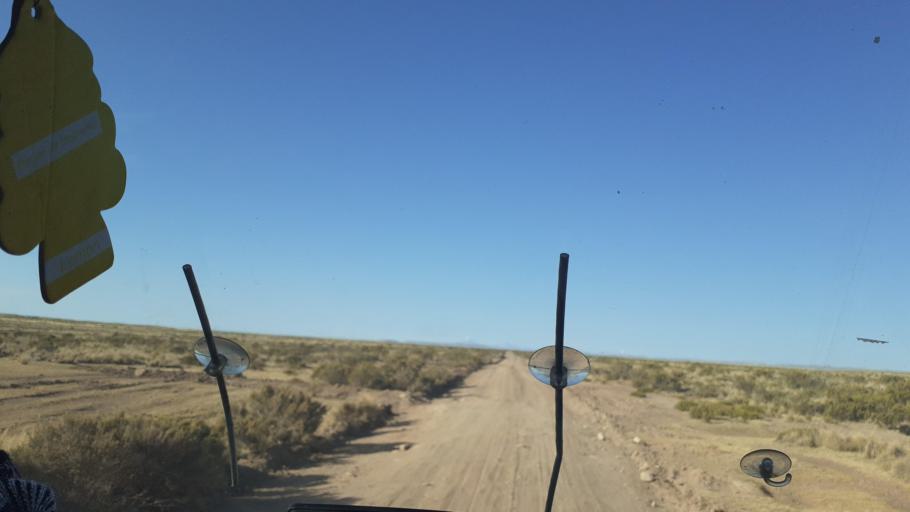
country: BO
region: La Paz
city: Tiahuanaco
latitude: -17.0498
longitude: -68.7568
